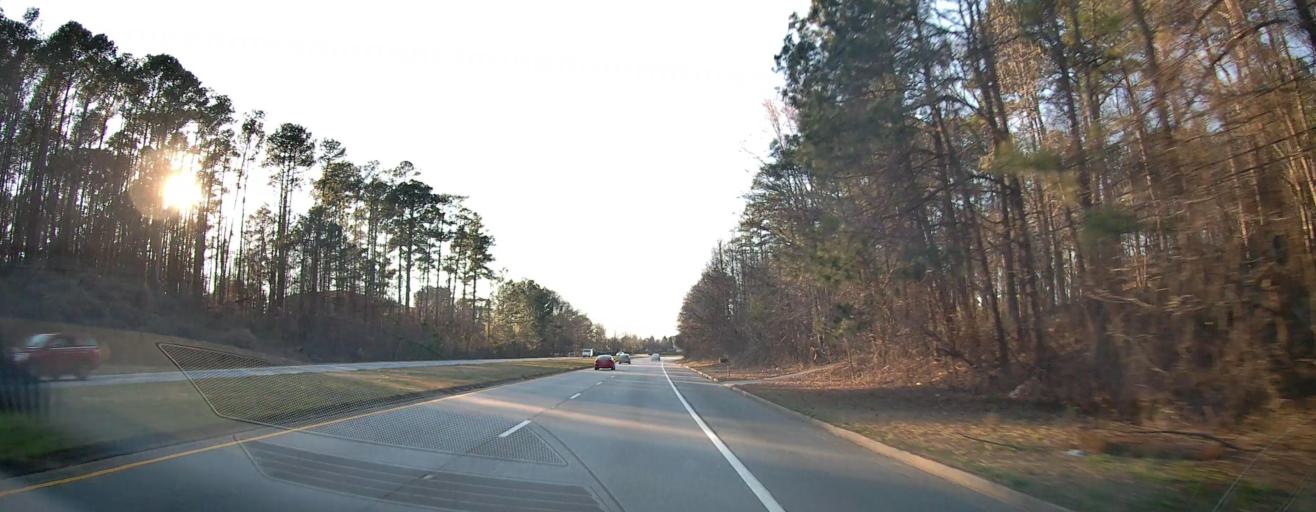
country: US
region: Georgia
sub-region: Fayette County
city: Fayetteville
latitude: 33.4485
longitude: -84.4978
